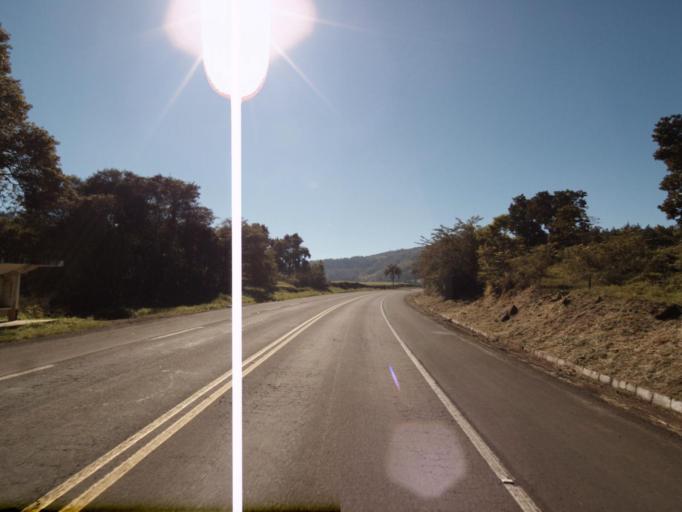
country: BR
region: Rio Grande do Sul
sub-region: Frederico Westphalen
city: Frederico Westphalen
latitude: -26.9814
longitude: -53.2206
